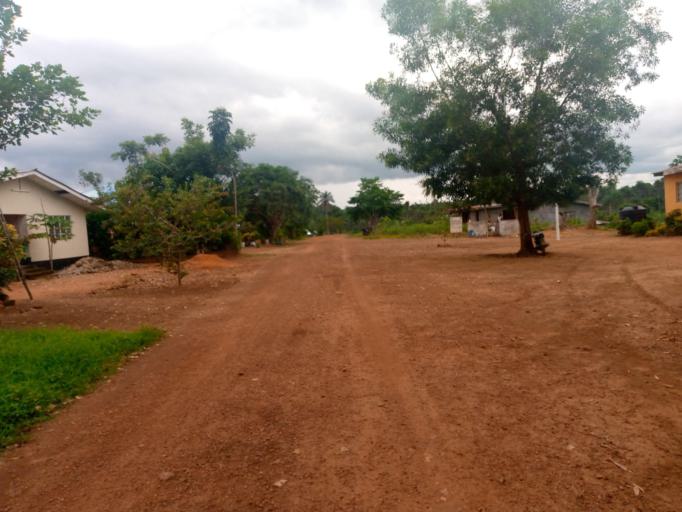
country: SL
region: Southern Province
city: Mogbwemo
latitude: 7.6176
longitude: -12.1778
